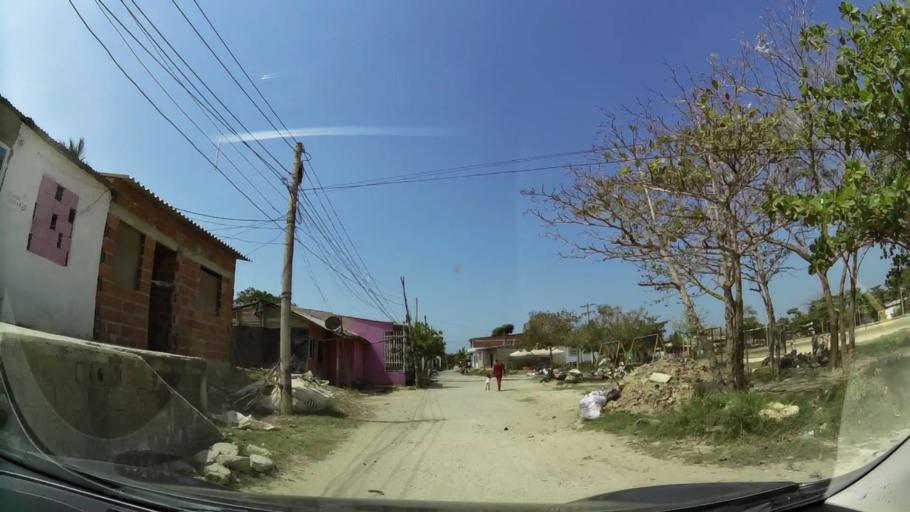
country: CO
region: Bolivar
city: Cartagena
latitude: 10.3450
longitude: -75.4892
